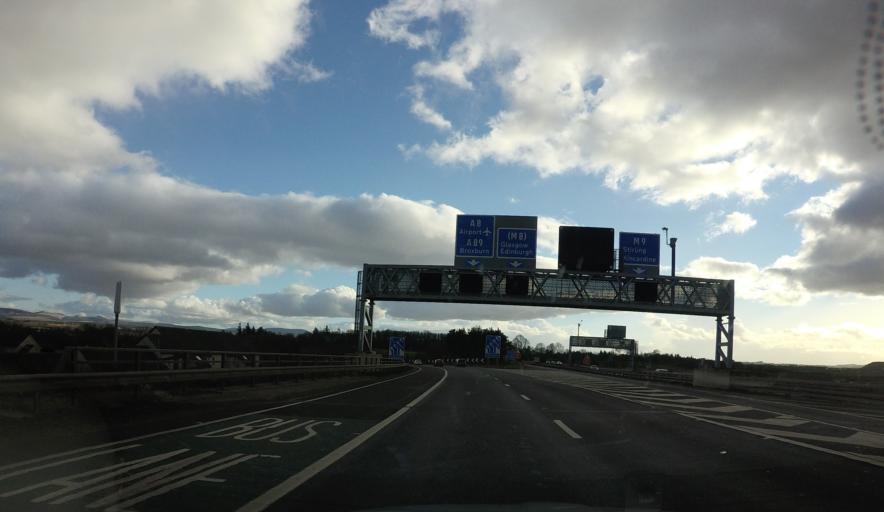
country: GB
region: Scotland
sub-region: Edinburgh
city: Kirkliston
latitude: 55.9575
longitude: -3.4170
